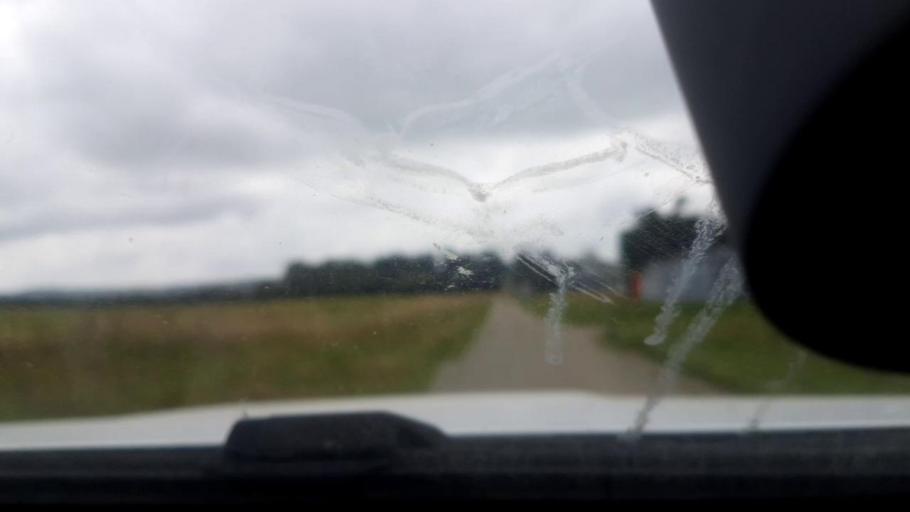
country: NZ
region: Canterbury
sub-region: Timaru District
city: Pleasant Point
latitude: -44.2246
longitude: 171.1641
